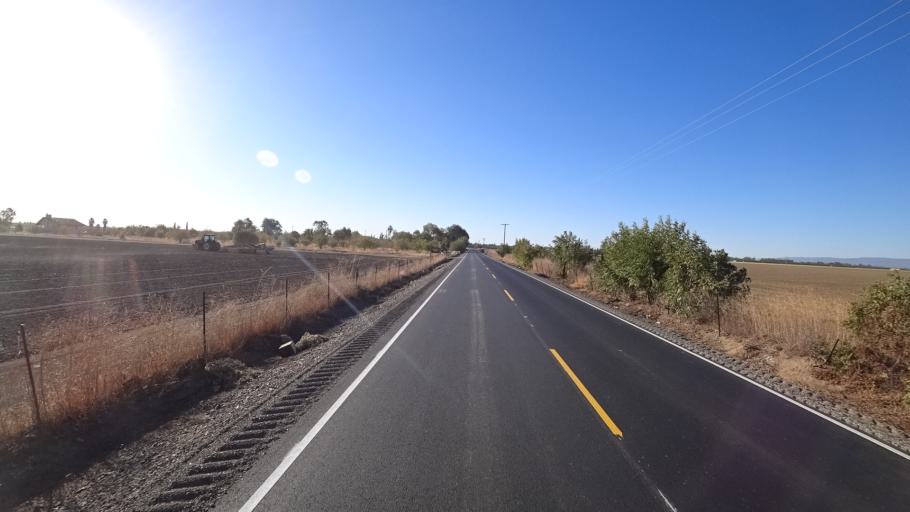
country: US
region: California
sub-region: Yolo County
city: Davis
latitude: 38.5693
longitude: -121.7860
